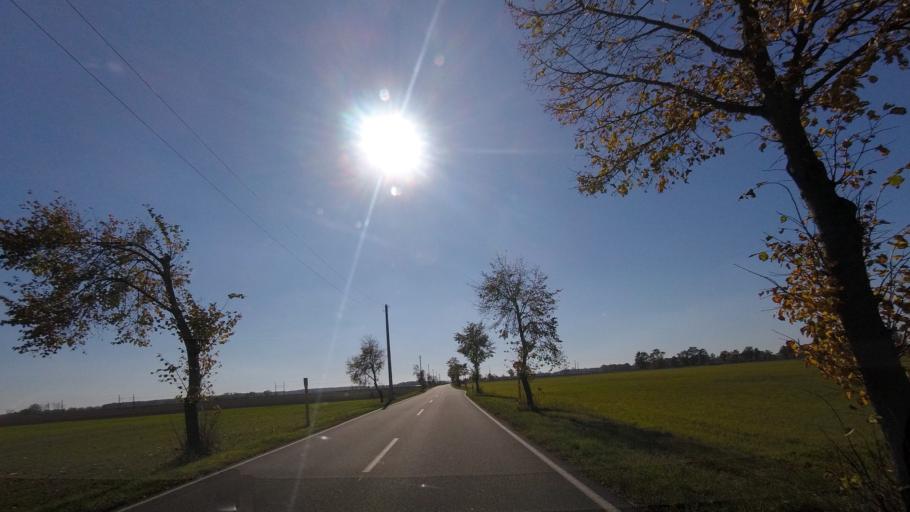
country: DE
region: Saxony-Anhalt
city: Muhlanger
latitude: 51.8513
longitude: 12.7709
